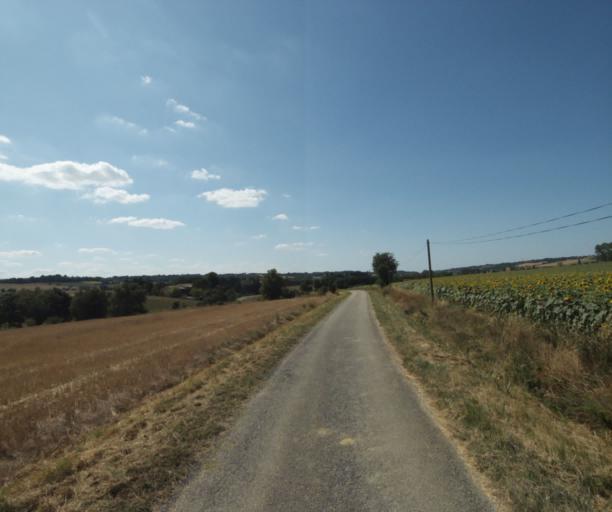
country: FR
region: Midi-Pyrenees
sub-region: Departement de la Haute-Garonne
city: Saint-Felix-Lauragais
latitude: 43.4760
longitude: 1.8923
